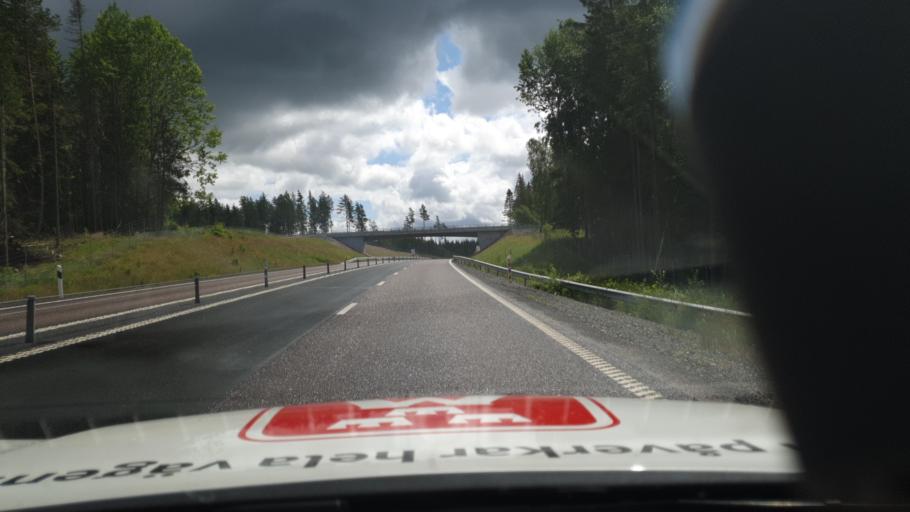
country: SE
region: Joenkoeping
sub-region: Mullsjo Kommun
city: Mullsjoe
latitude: 57.8950
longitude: 13.8787
